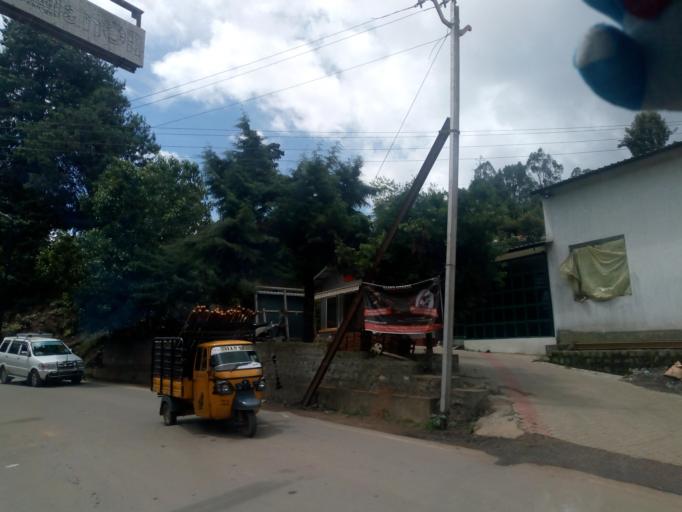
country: IN
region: Tamil Nadu
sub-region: Nilgiri
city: Ooty
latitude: 11.4022
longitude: 76.6959
